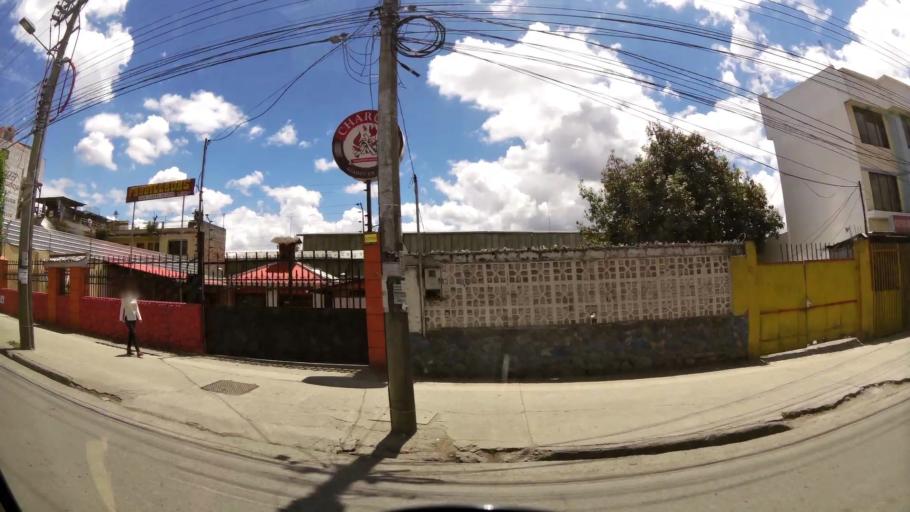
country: EC
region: Azuay
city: Cuenca
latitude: -2.9125
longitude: -79.0363
